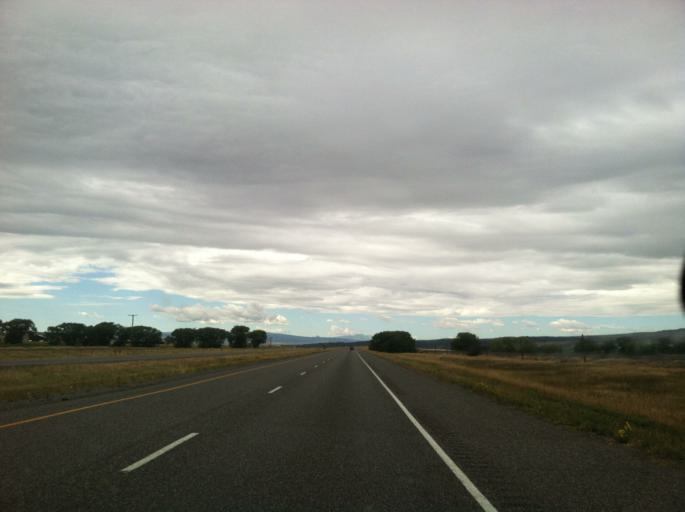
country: US
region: Montana
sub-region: Park County
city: Livingston
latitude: 45.7011
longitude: -110.3271
